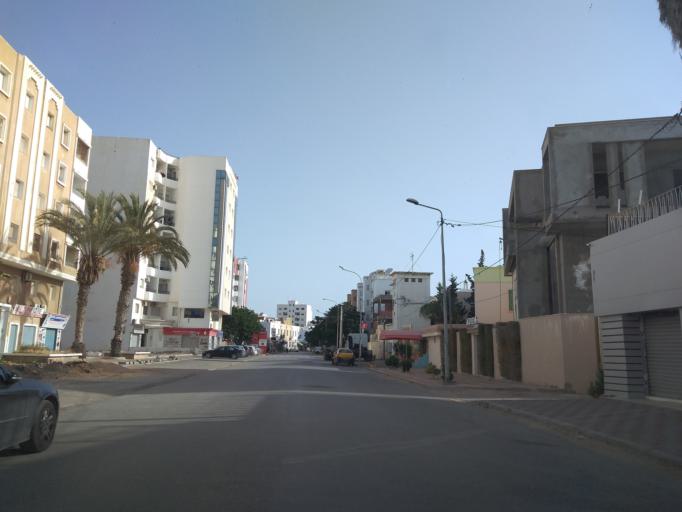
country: TN
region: Safaqis
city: Sfax
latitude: 34.7300
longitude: 10.7550
